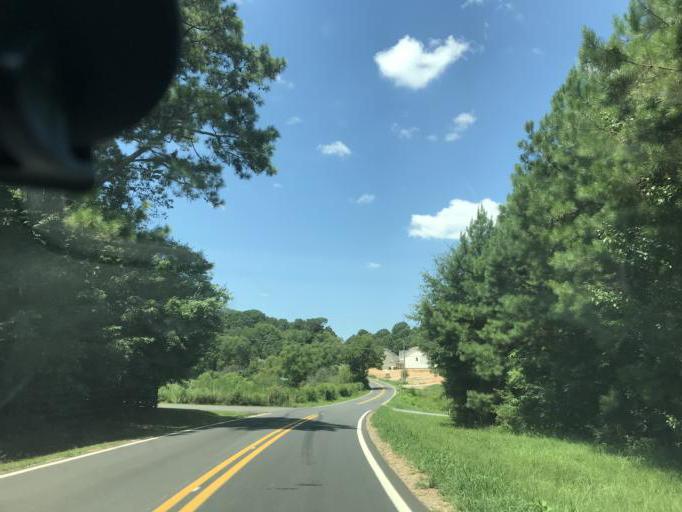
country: US
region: Georgia
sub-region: Forsyth County
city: Cumming
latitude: 34.2681
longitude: -84.2536
